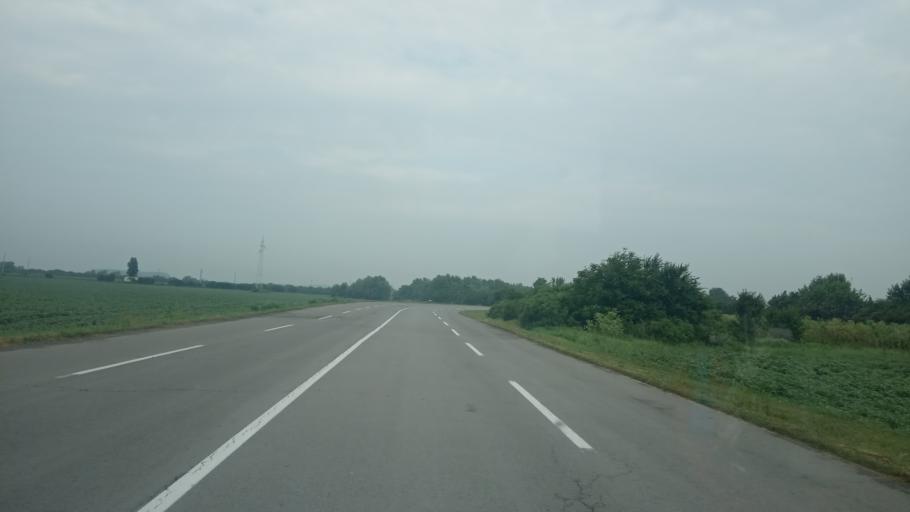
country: RS
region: Central Serbia
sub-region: Belgrade
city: Zemun
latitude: 44.9212
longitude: 20.4443
